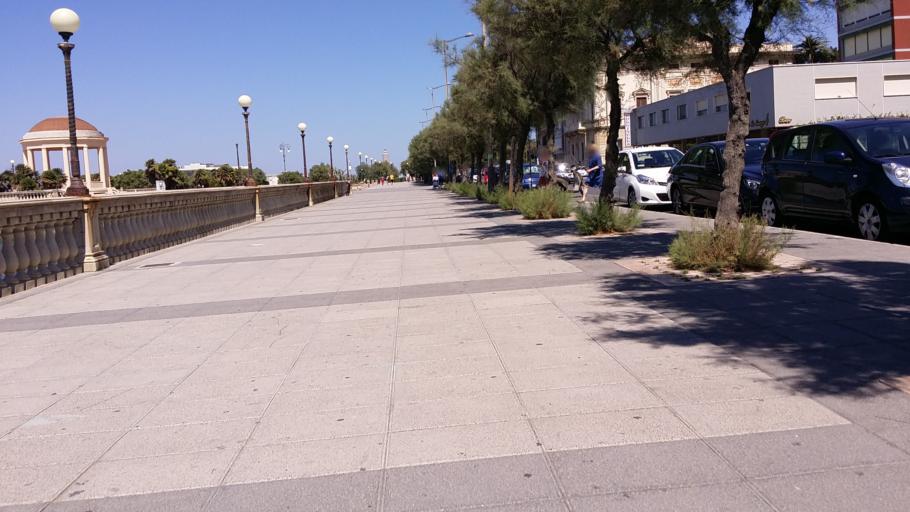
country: IT
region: Tuscany
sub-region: Provincia di Livorno
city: Livorno
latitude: 43.5327
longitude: 10.3022
